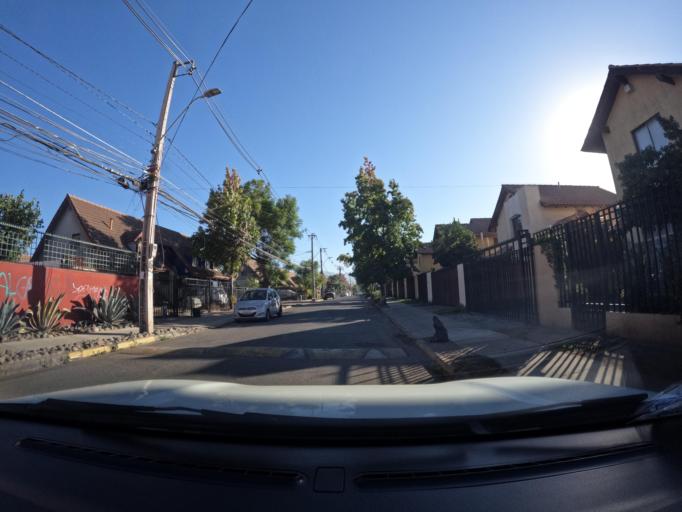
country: CL
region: Santiago Metropolitan
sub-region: Provincia de Santiago
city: Villa Presidente Frei, Nunoa, Santiago, Chile
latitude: -33.4801
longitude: -70.5474
